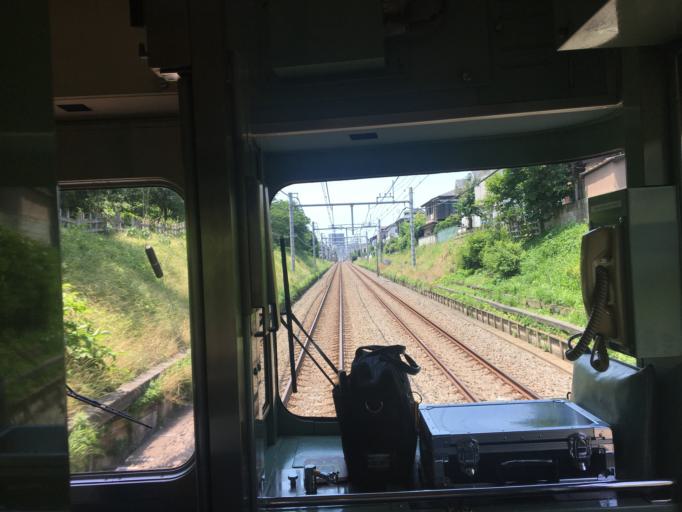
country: JP
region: Tokyo
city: Tanashicho
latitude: 35.7657
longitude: 139.5287
